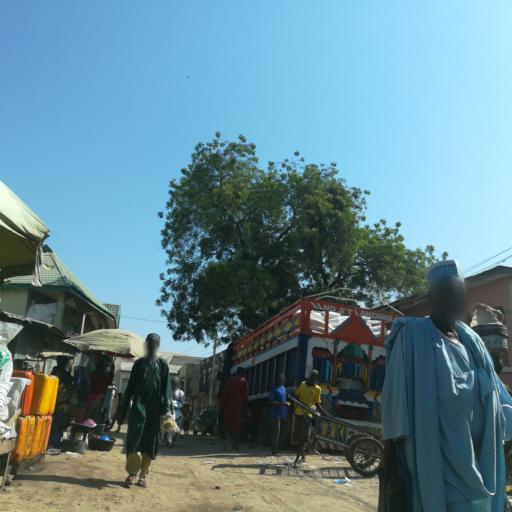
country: NG
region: Kano
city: Kano
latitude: 12.0093
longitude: 8.5347
